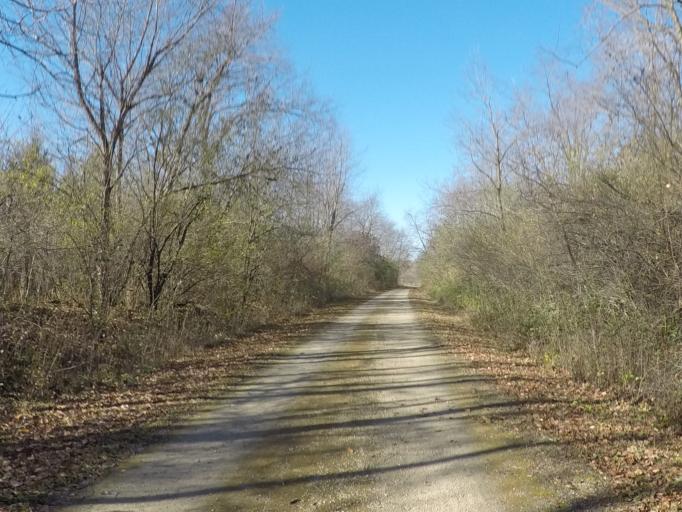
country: US
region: Wisconsin
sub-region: Dane County
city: Deerfield
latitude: 43.0422
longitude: -89.0426
